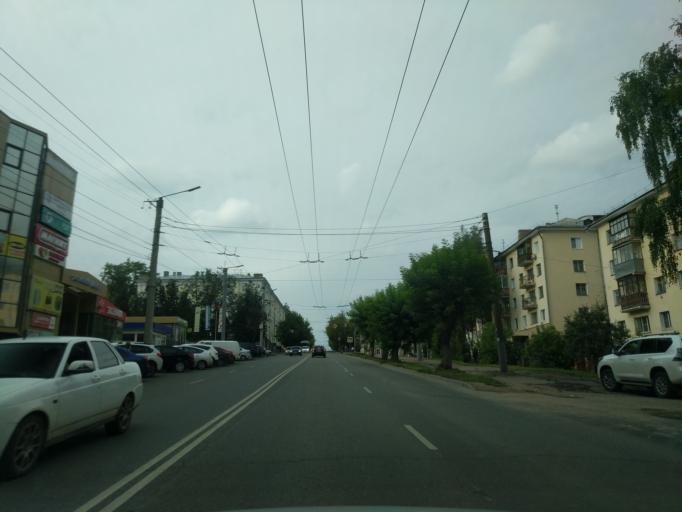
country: RU
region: Kirov
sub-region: Kirovo-Chepetskiy Rayon
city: Kirov
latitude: 58.5905
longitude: 49.6692
